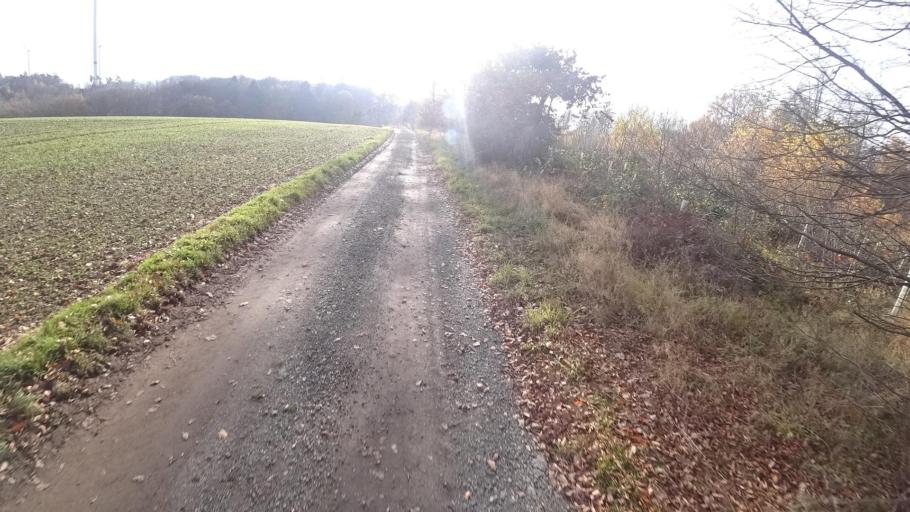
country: DE
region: Rheinland-Pfalz
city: Hungenroth
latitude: 50.1373
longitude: 7.5947
